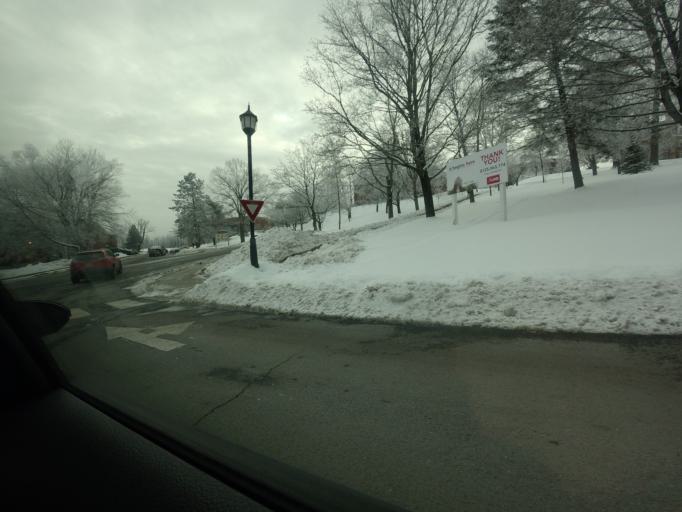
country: CA
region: New Brunswick
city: Fredericton
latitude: 45.9490
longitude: -66.6399
